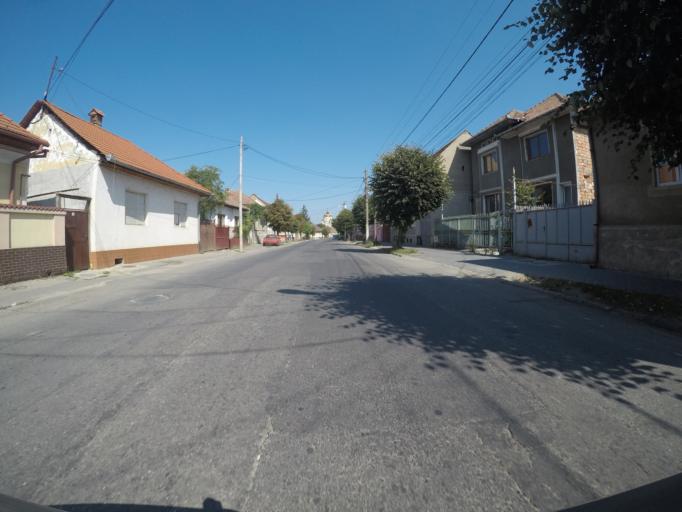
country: RO
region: Brasov
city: Fogarasch
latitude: 45.8385
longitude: 24.9741
